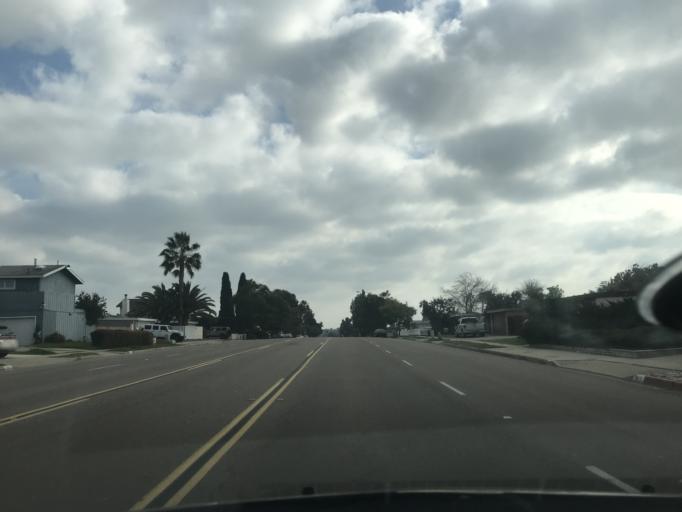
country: US
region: California
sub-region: San Diego County
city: San Diego
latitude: 32.7981
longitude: -117.1262
